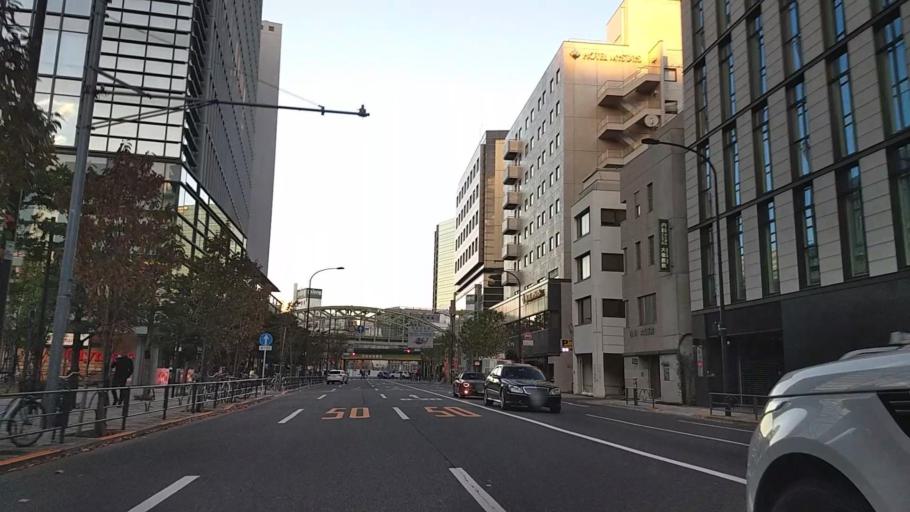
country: JP
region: Tokyo
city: Tokyo
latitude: 35.6969
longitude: 139.7678
